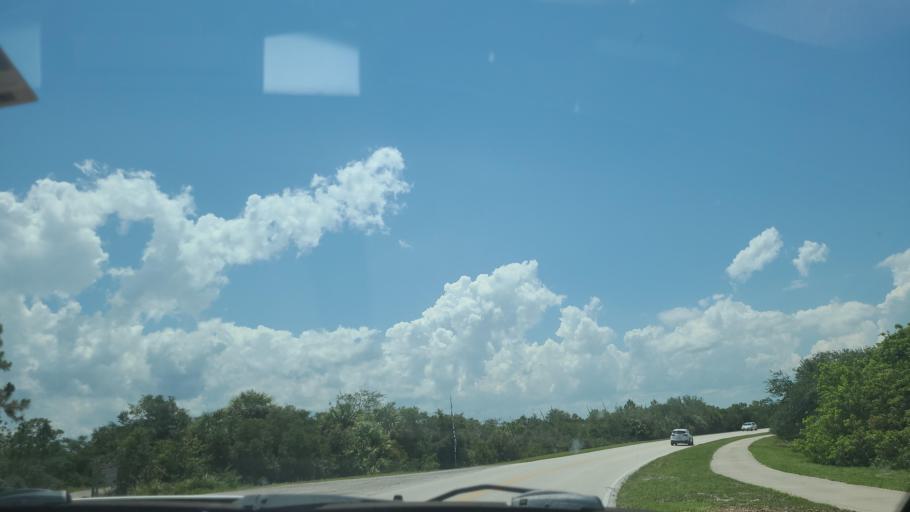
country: US
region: Florida
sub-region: Brevard County
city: Grant-Valkaria
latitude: 27.9638
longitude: -80.5510
